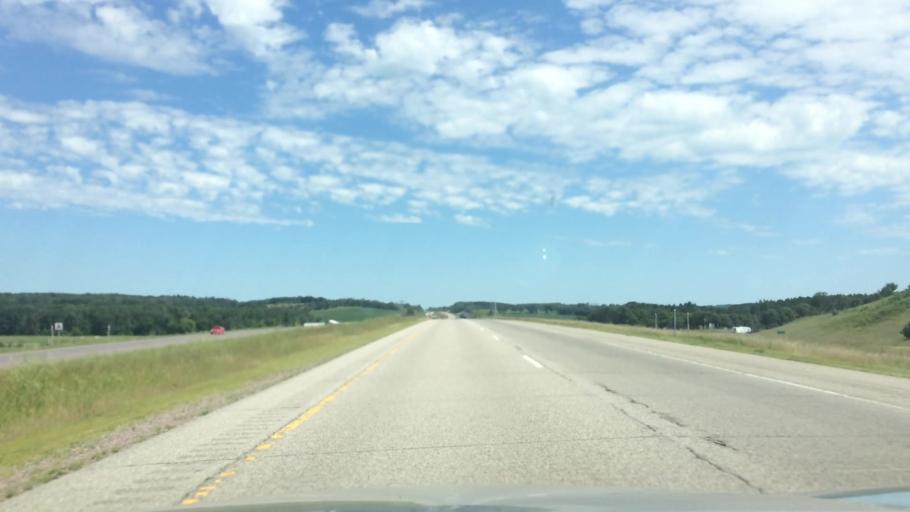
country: US
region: Wisconsin
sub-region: Marquette County
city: Westfield
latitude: 43.7877
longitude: -89.4834
